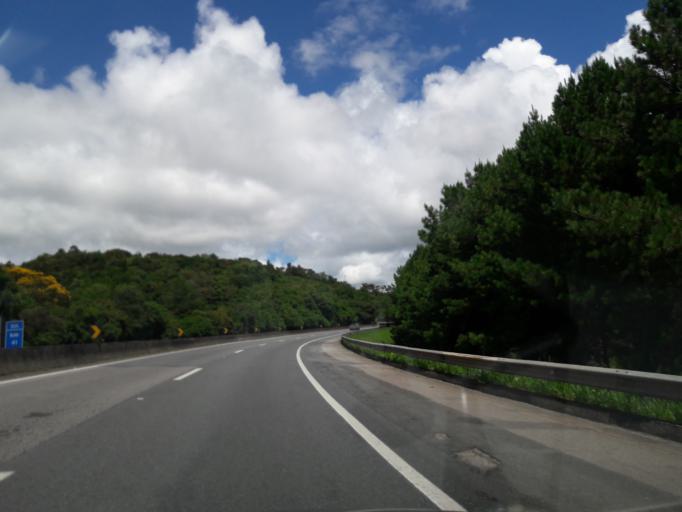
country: BR
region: Parana
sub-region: Campina Grande Do Sul
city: Campina Grande do Sul
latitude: -25.1746
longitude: -48.8689
